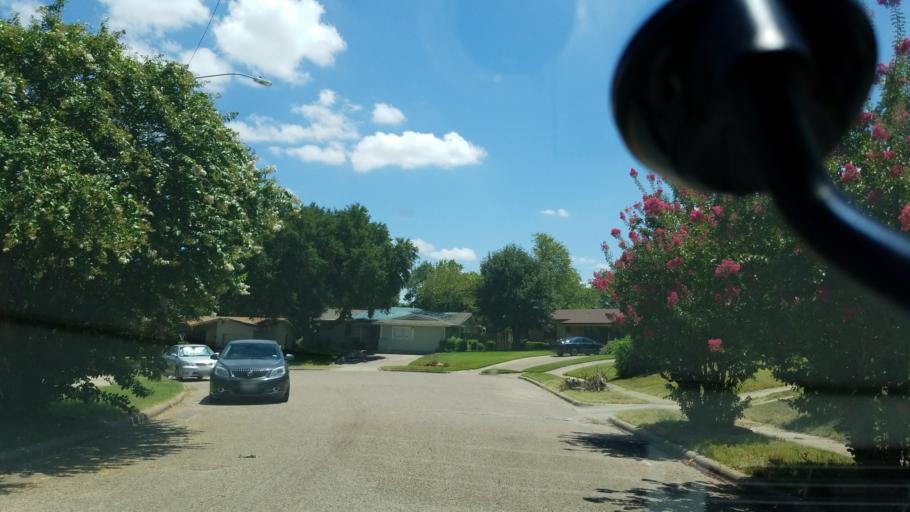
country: US
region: Texas
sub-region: Dallas County
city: Cockrell Hill
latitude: 32.6942
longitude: -96.8158
